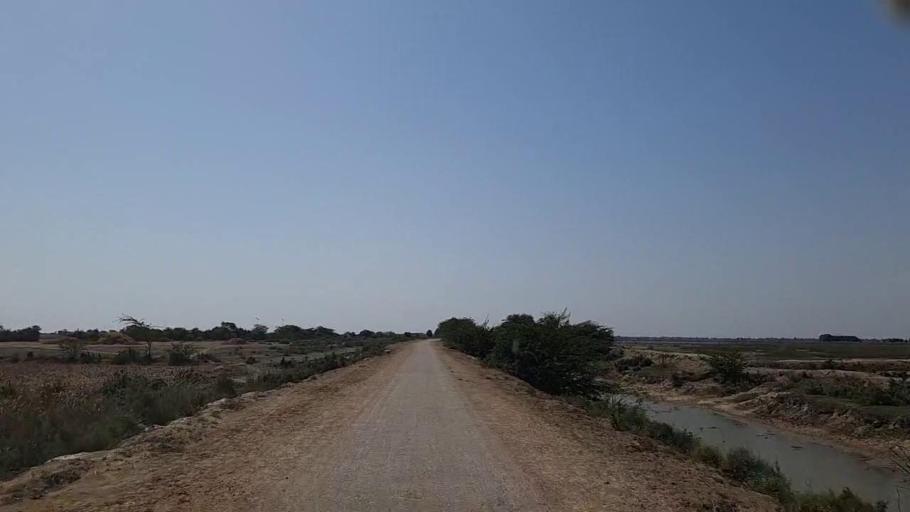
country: PK
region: Sindh
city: Mirpur Batoro
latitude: 24.6750
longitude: 68.3053
